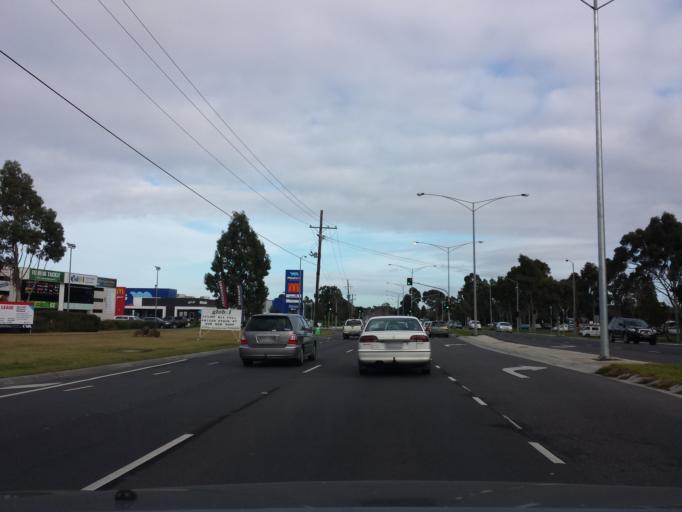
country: AU
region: Victoria
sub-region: Knox
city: Knoxfield
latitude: -37.8976
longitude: 145.2441
